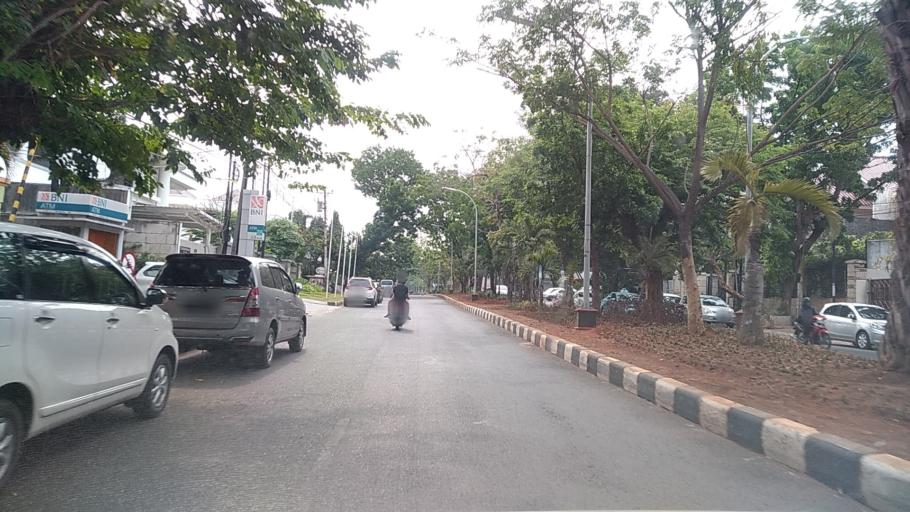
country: ID
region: Central Java
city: Semarang
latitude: -7.0158
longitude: 110.4230
